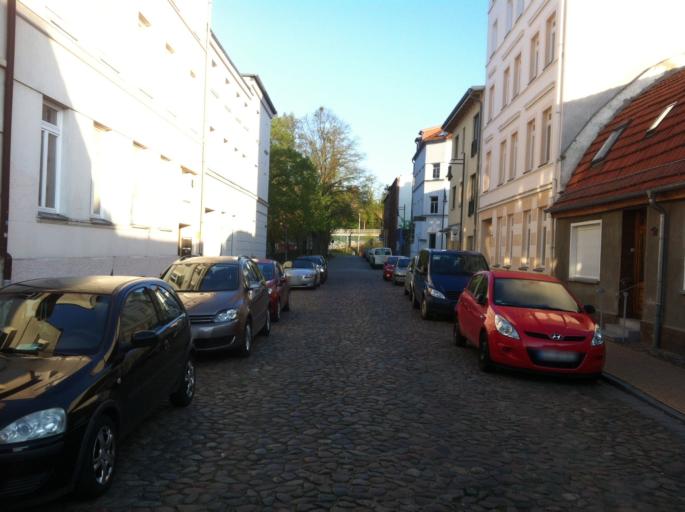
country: DE
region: Mecklenburg-Vorpommern
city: Feldstadt
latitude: 53.6216
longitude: 11.4040
